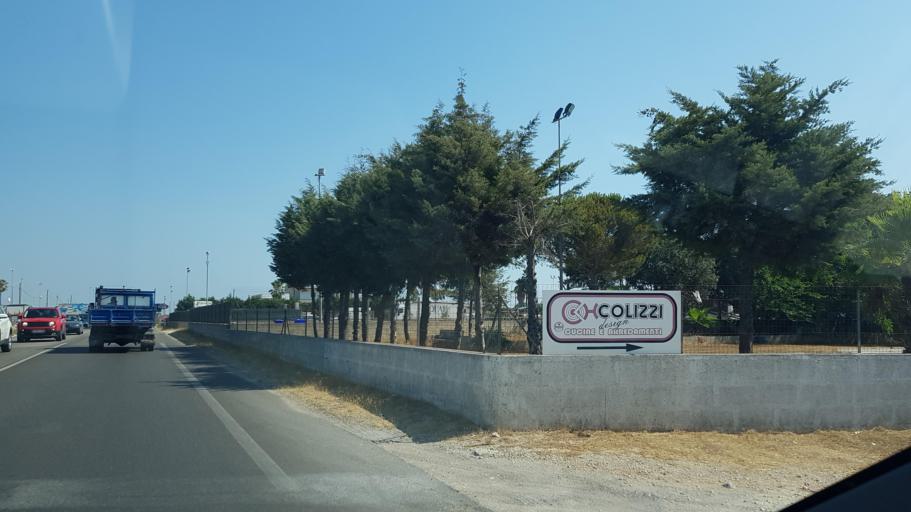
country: IT
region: Apulia
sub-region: Provincia di Lecce
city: Nociglia
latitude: 40.0109
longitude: 18.3241
